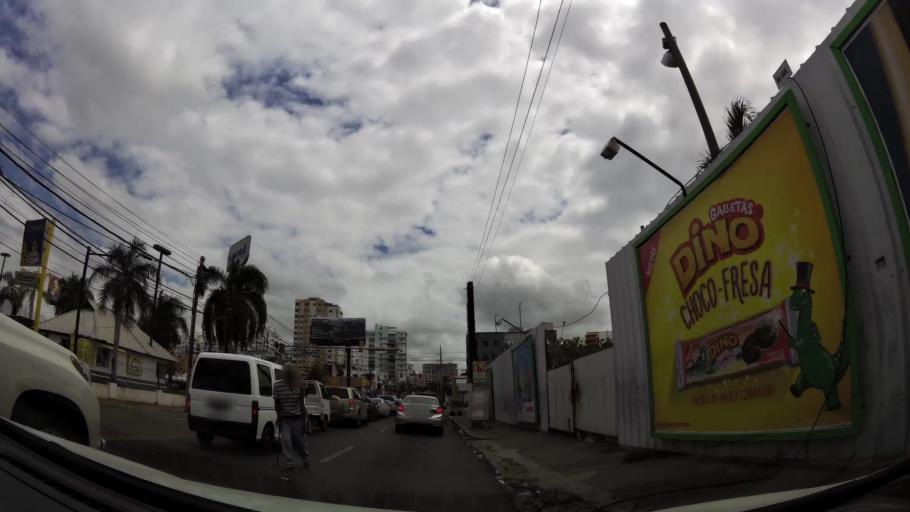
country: DO
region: Nacional
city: La Julia
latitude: 18.4786
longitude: -69.9457
